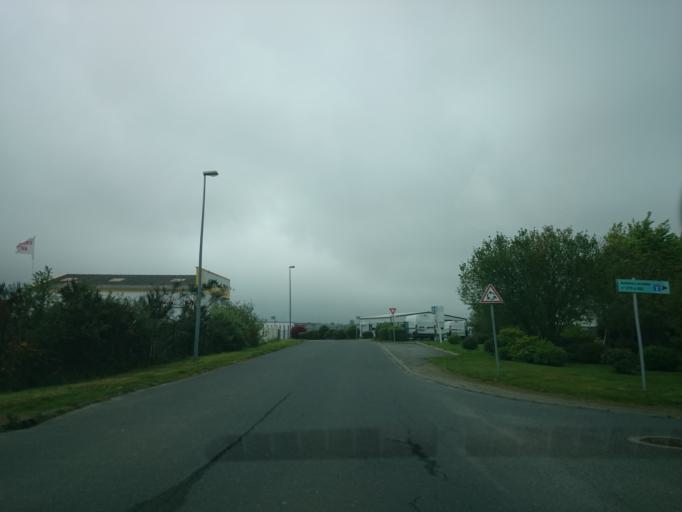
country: FR
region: Brittany
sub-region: Departement du Finistere
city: Gouesnou
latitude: 48.4567
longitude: -4.4502
